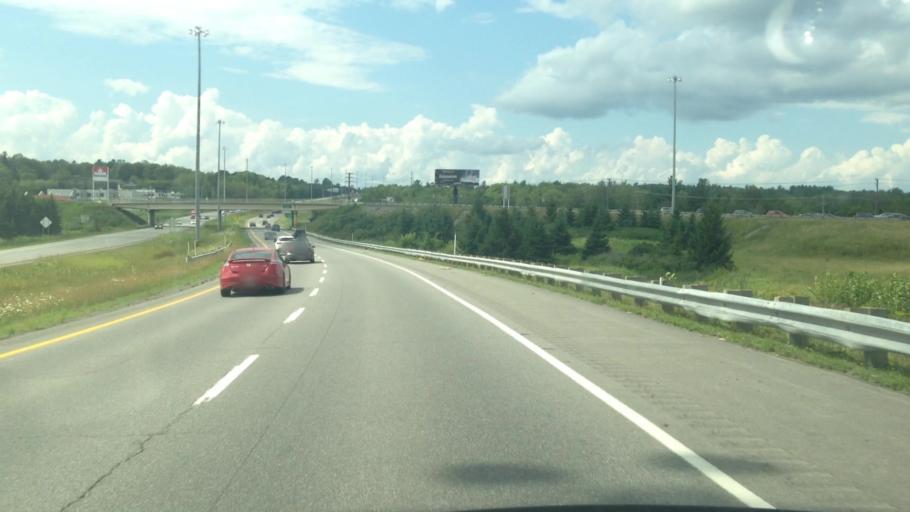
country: CA
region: Quebec
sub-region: Laurentides
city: Saint-Jerome
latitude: 45.7947
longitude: -74.0223
